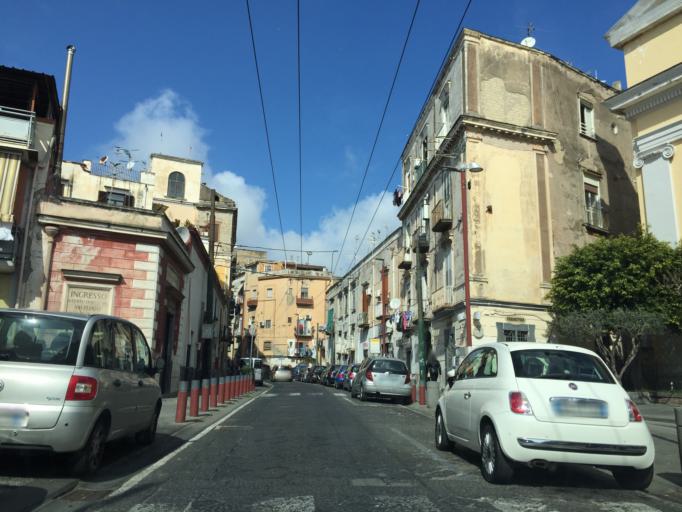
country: IT
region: Campania
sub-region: Provincia di Napoli
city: Portici
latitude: 40.8077
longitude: 14.3483
